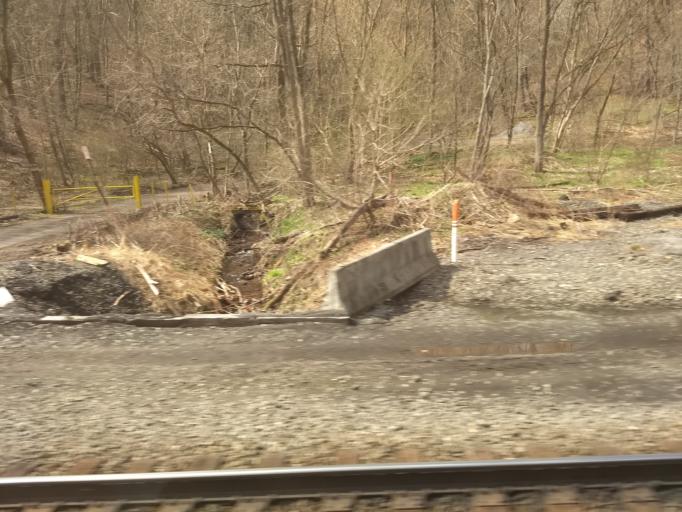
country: US
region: Pennsylvania
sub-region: Blair County
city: Tyrone
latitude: 40.6654
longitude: -78.2297
